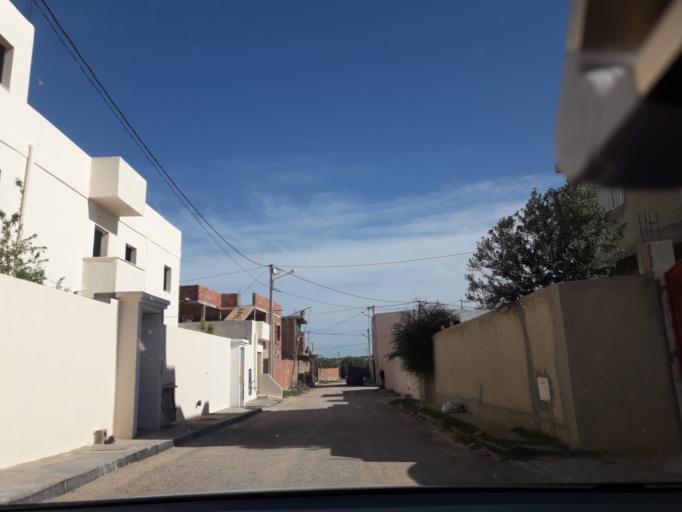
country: TN
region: Safaqis
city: Sfax
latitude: 34.7394
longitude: 10.5185
